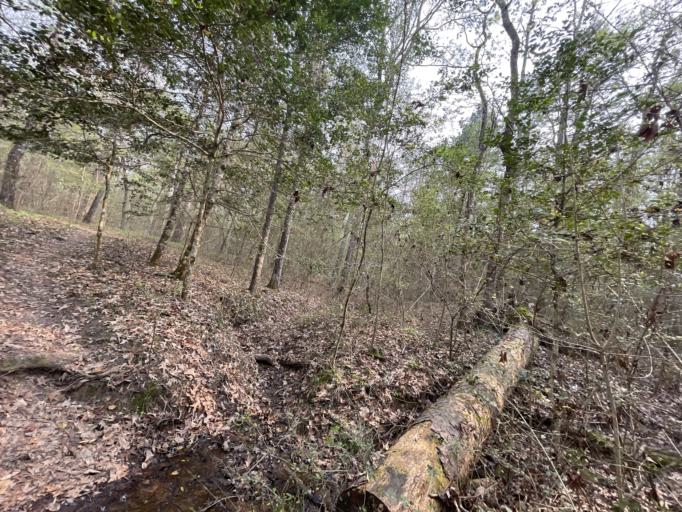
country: US
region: Texas
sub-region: Walker County
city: Huntsville
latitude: 30.6594
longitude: -95.4847
